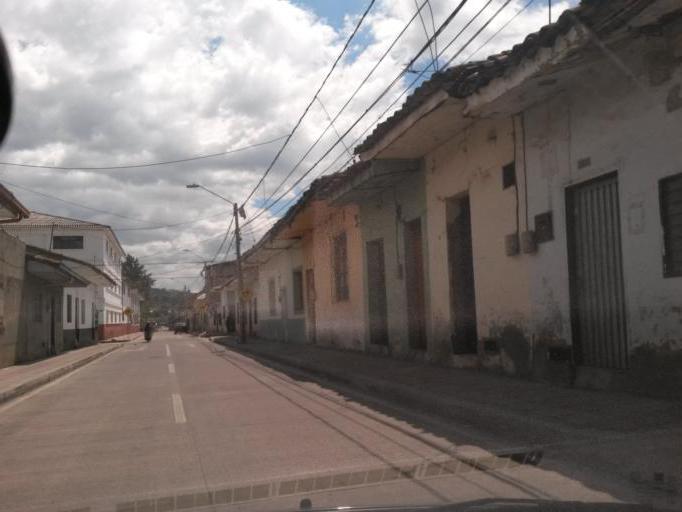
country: CO
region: Cauca
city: Popayan
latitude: 2.4360
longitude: -76.6060
